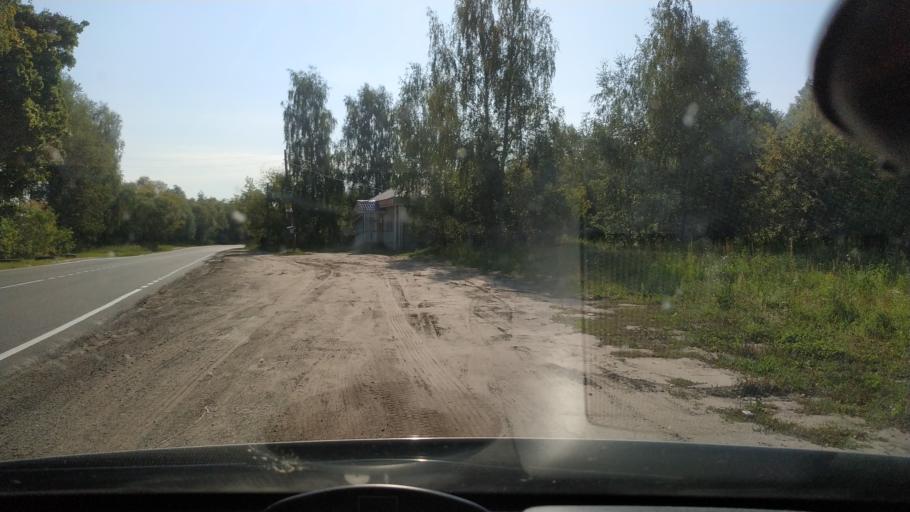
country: RU
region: Rjazan
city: Spas-Klepiki
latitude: 55.2202
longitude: 40.0897
